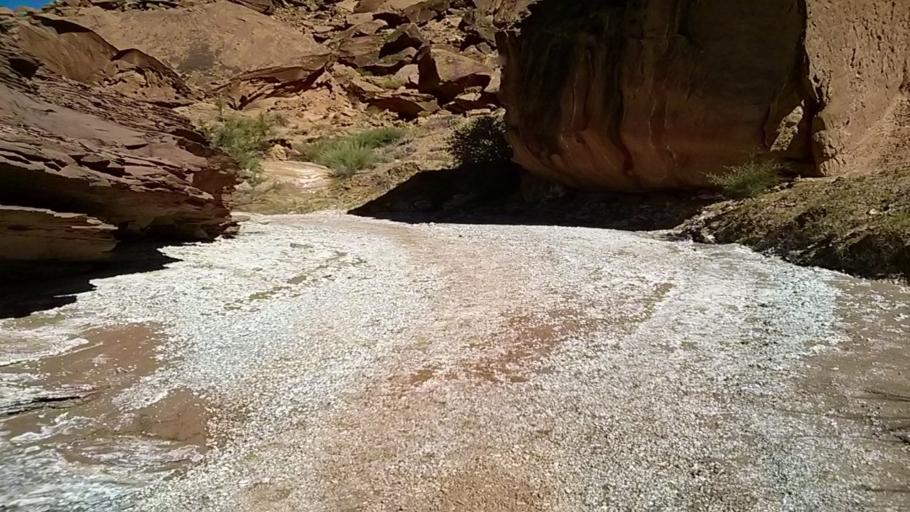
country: US
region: Utah
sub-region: Grand County
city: Moab
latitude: 38.4439
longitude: -109.9488
